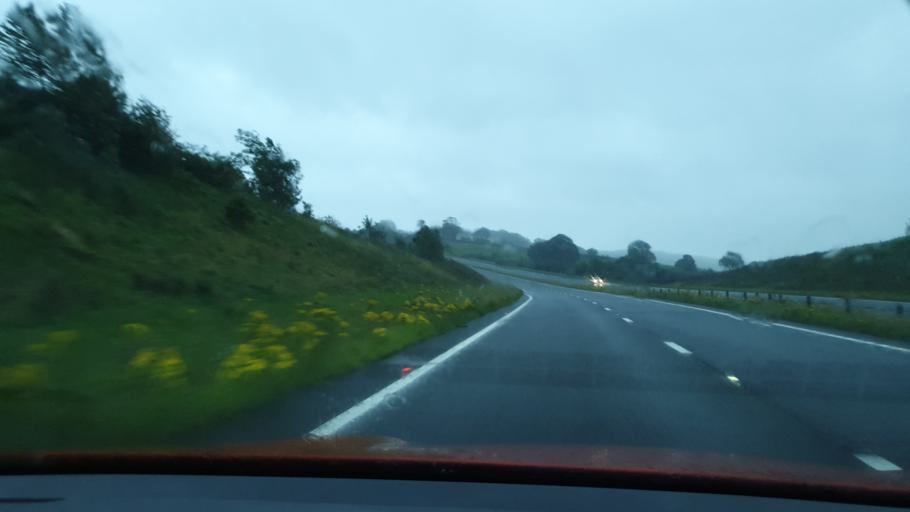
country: GB
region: England
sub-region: Cumbria
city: Grange-over-Sands
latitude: 54.2411
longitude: -2.9269
